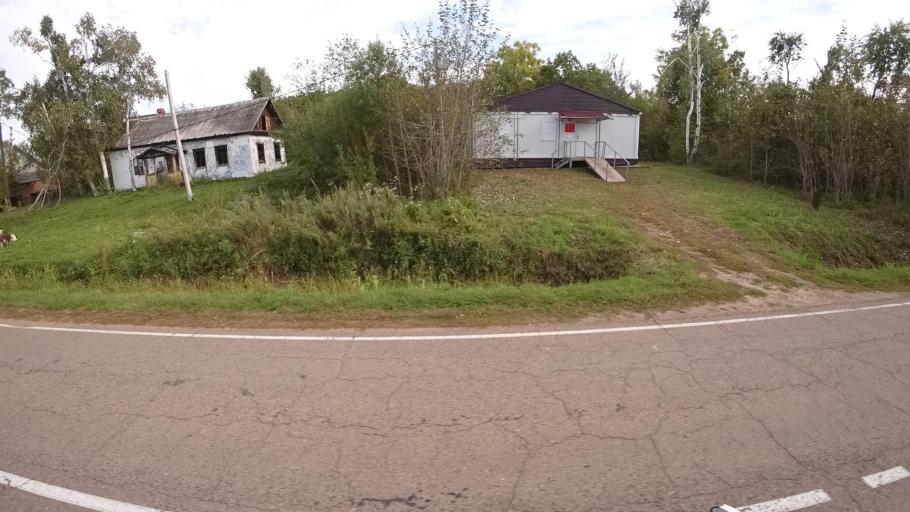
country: RU
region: Primorskiy
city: Dostoyevka
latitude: 44.3286
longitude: 133.4781
